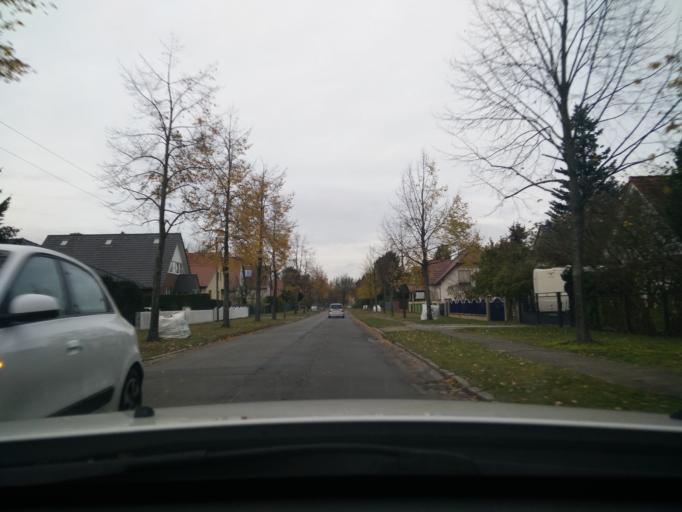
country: DE
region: Berlin
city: Staaken
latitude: 52.5611
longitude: 13.1307
